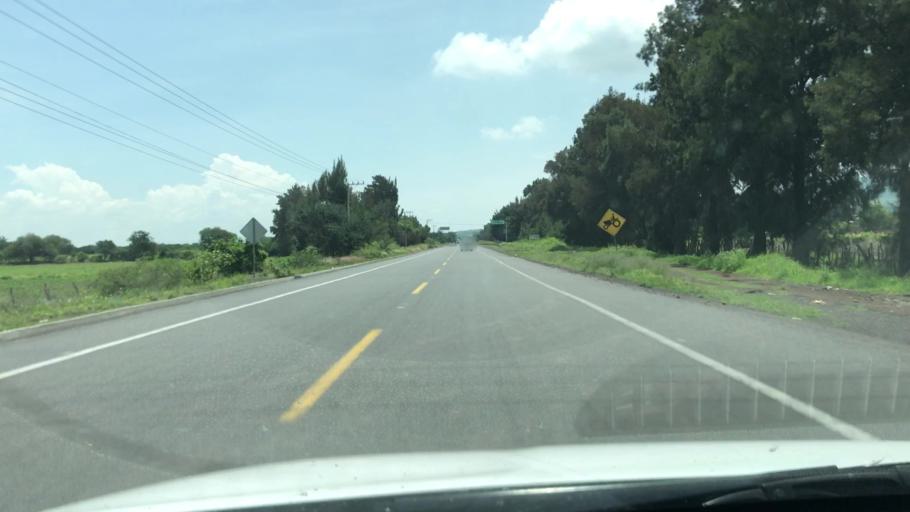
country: MX
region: Michoacan
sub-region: Yurecuaro
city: Yurecuaro
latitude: 20.3399
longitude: -102.1773
